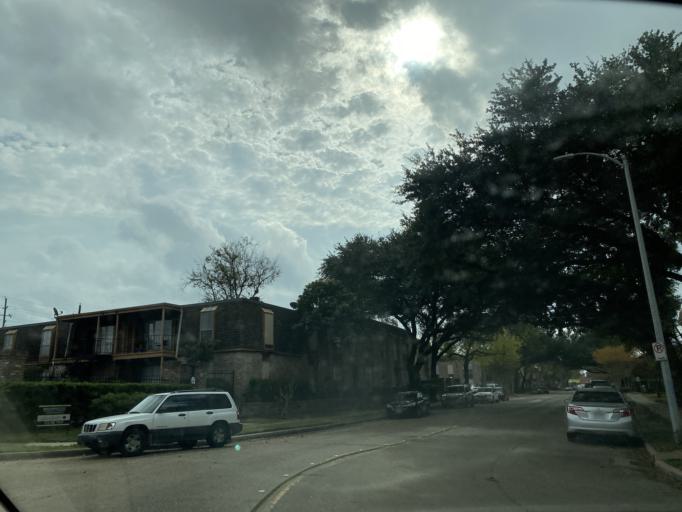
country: US
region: Texas
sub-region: Harris County
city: Piney Point Village
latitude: 29.7424
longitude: -95.4967
